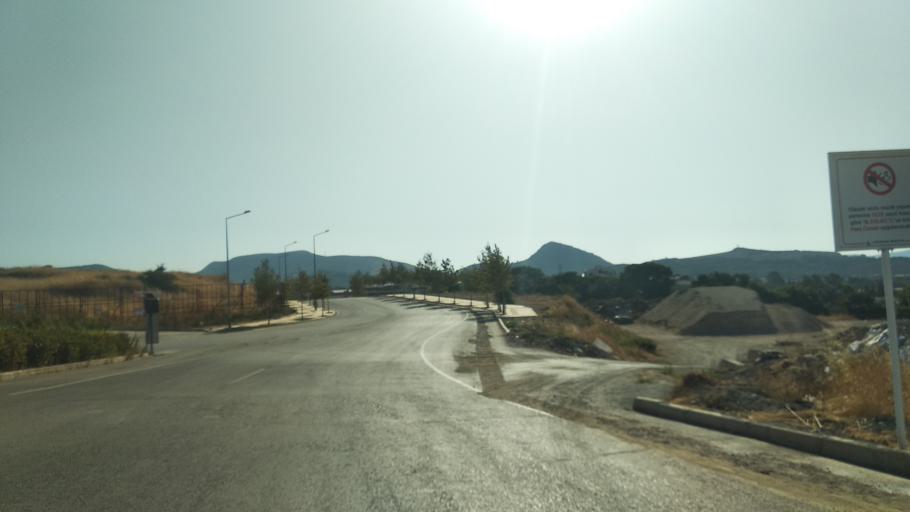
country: TR
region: Izmir
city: Urla
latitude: 38.3603
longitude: 26.8786
